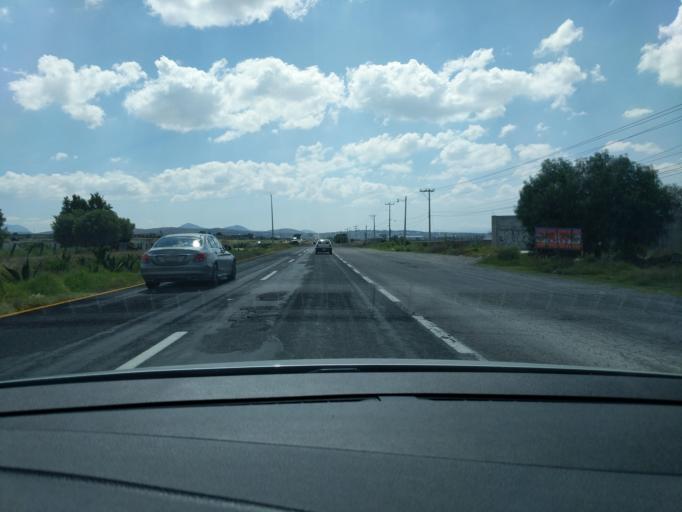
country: MX
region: Hidalgo
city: Zempoala
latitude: 19.9577
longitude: -98.6938
